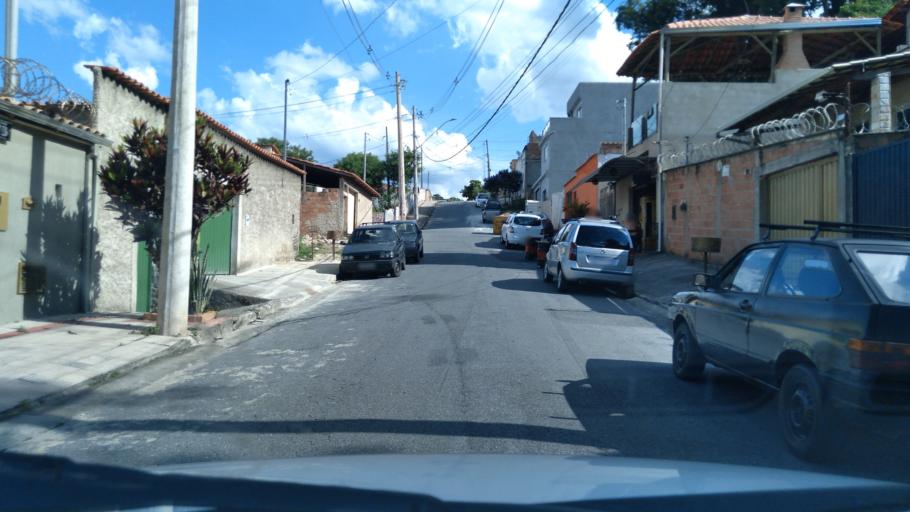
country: BR
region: Minas Gerais
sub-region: Belo Horizonte
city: Belo Horizonte
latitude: -19.8573
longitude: -43.8797
